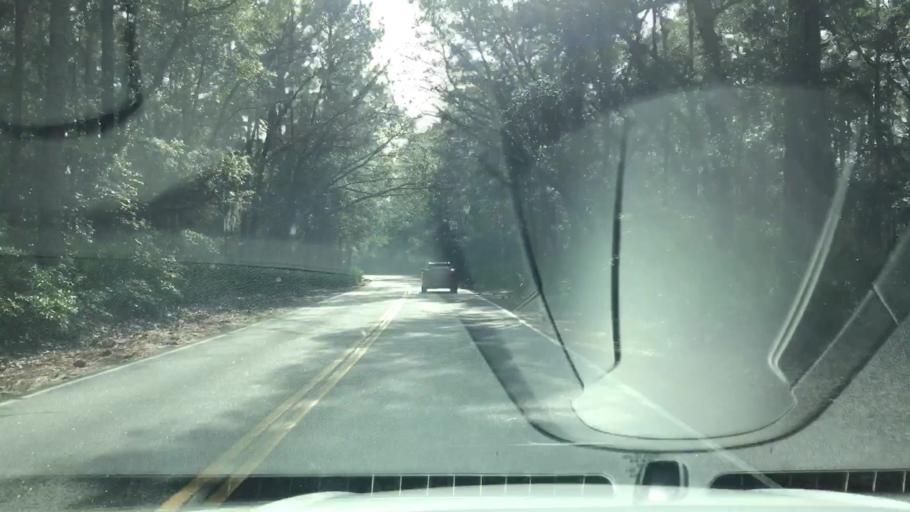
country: US
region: South Carolina
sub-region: Beaufort County
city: Hilton Head Island
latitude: 32.2356
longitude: -80.7239
